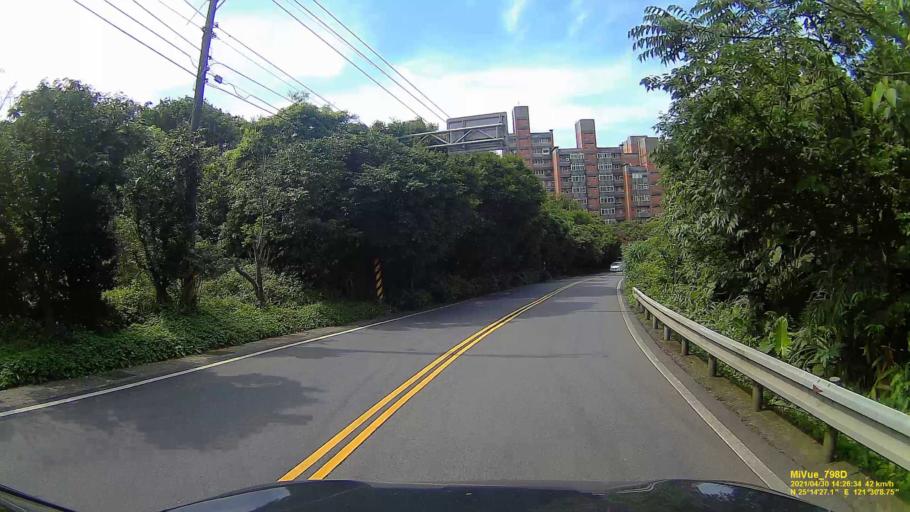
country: TW
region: Taipei
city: Taipei
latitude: 25.2410
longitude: 121.5024
